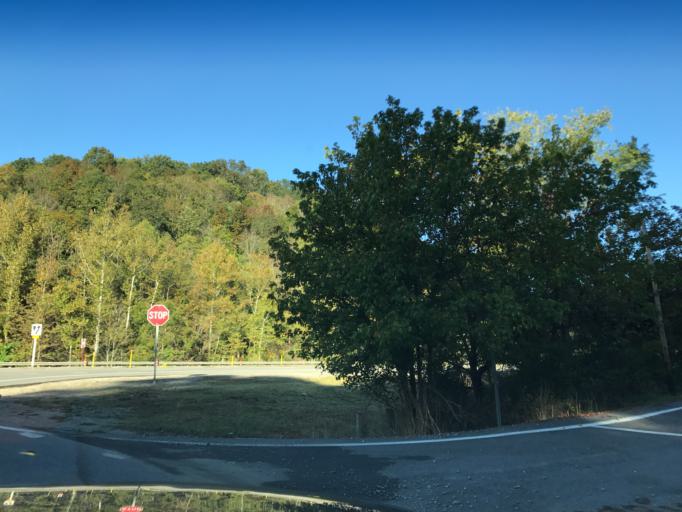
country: US
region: Ohio
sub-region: Washington County
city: Newport
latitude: 39.2421
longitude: -81.2285
